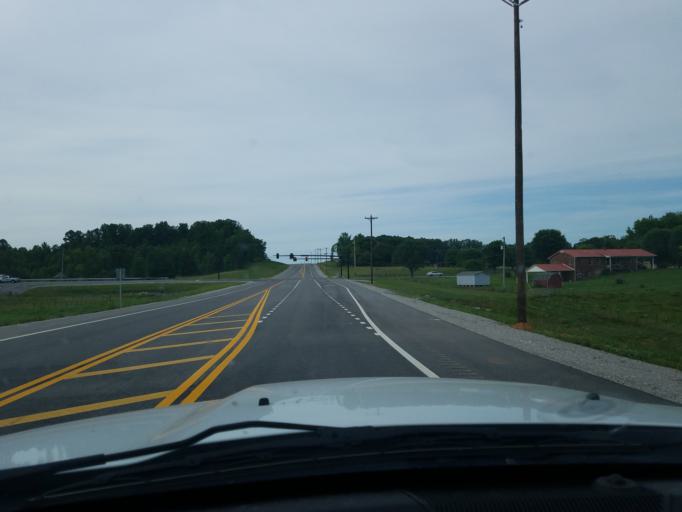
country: US
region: Tennessee
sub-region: Putnam County
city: Cookeville
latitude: 36.1590
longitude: -85.5641
